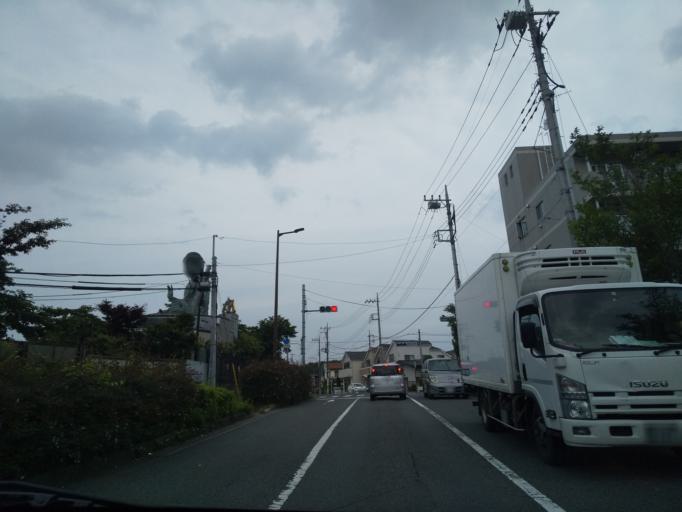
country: JP
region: Tokyo
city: Hino
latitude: 35.6628
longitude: 139.3895
